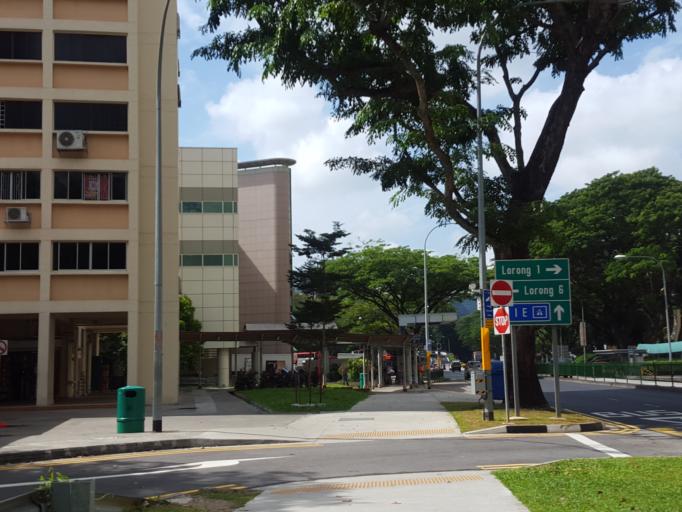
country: SG
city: Singapore
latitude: 1.3338
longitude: 103.8469
